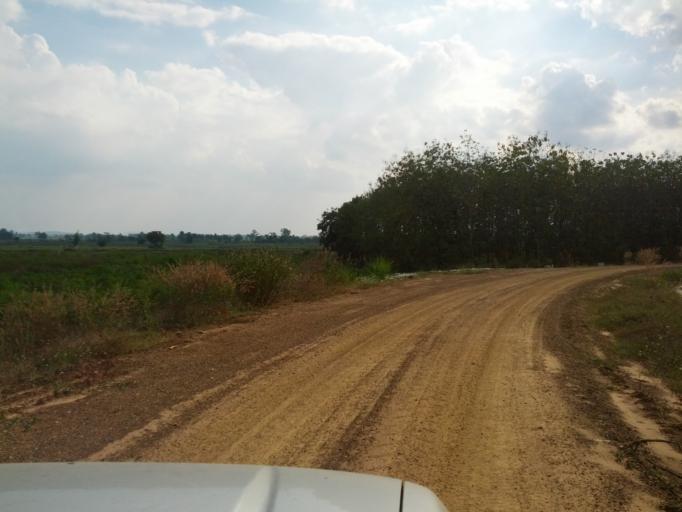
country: TH
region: Sukhothai
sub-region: Amphoe Si Satchanalai
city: Si Satchanalai
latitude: 17.4645
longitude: 99.6999
